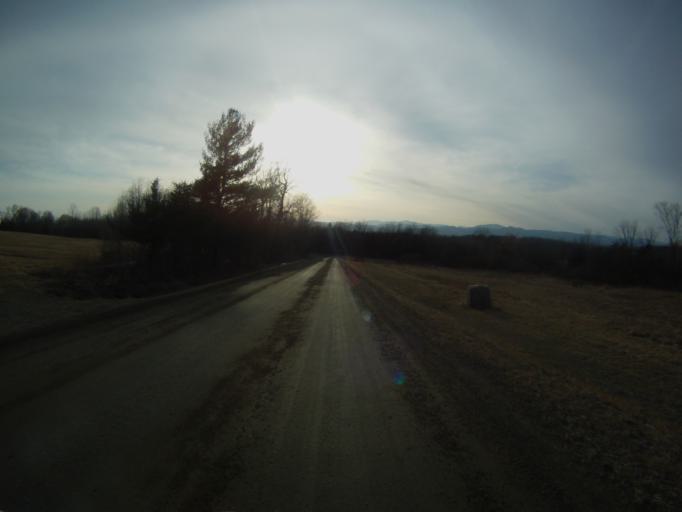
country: US
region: Vermont
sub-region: Addison County
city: Middlebury (village)
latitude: 44.0395
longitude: -73.2914
